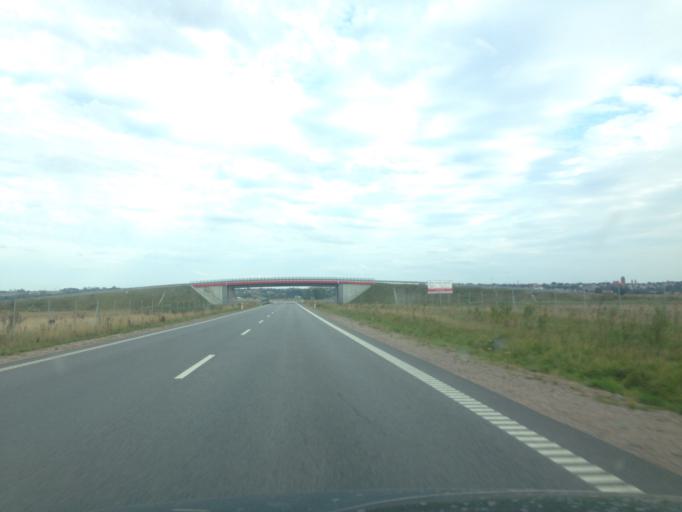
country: PL
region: Pomeranian Voivodeship
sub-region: Powiat kwidzynski
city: Kwidzyn
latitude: 53.7560
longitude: 18.8929
